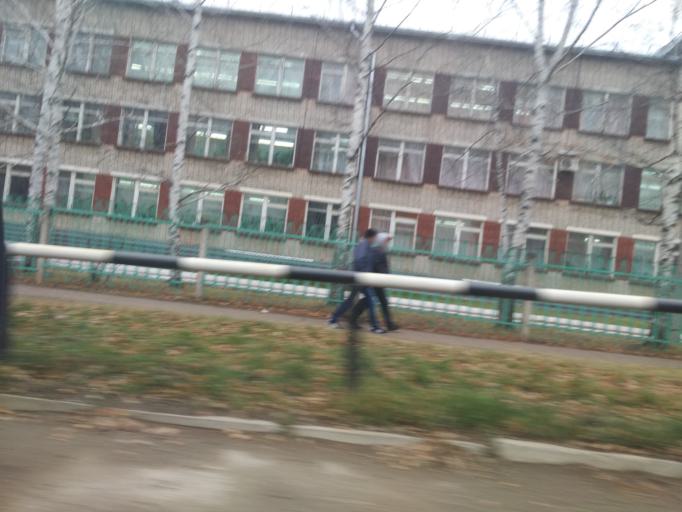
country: RU
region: Kirov
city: Vyatskiye Polyany
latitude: 56.2289
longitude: 51.0755
